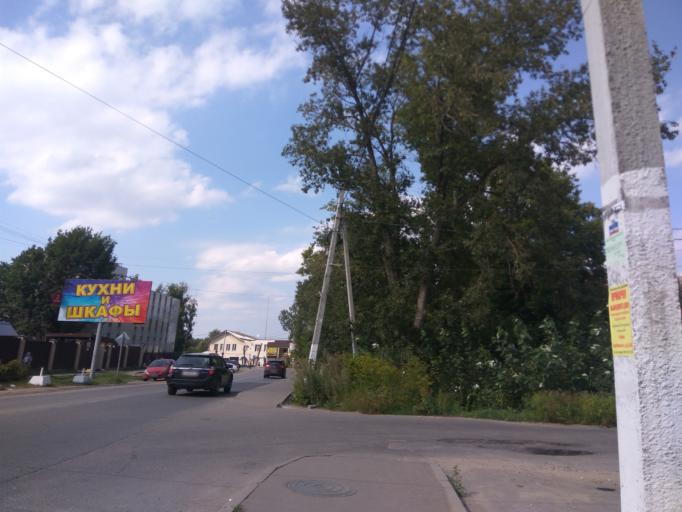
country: RU
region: Moskovskaya
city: Kubinka
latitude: 55.5774
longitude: 36.6942
